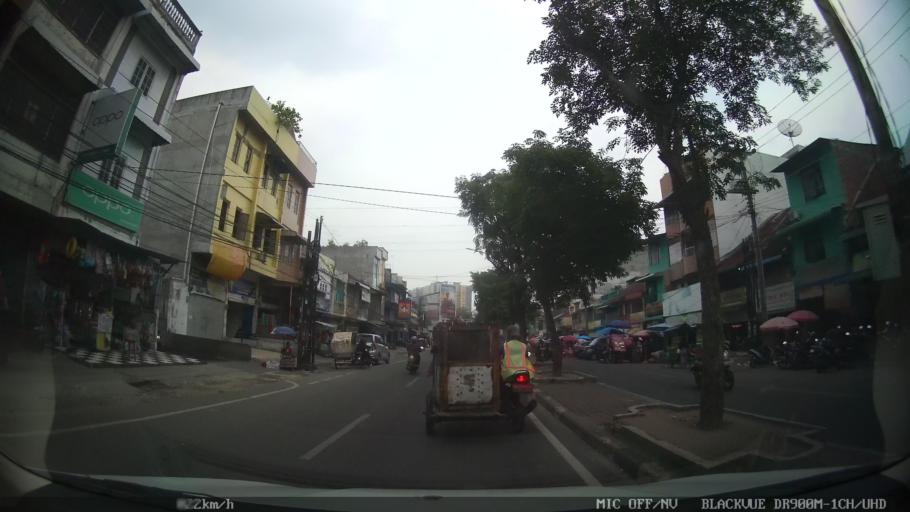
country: ID
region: North Sumatra
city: Medan
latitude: 3.5810
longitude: 98.7038
